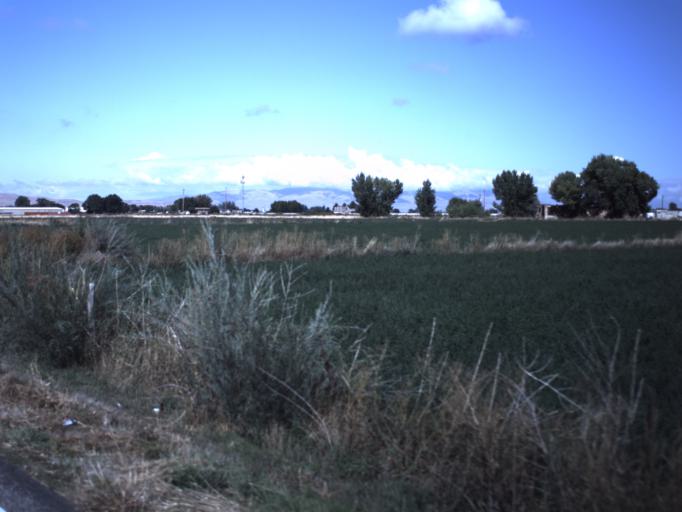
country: US
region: Utah
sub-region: Utah County
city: Benjamin
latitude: 40.0983
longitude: -111.7031
